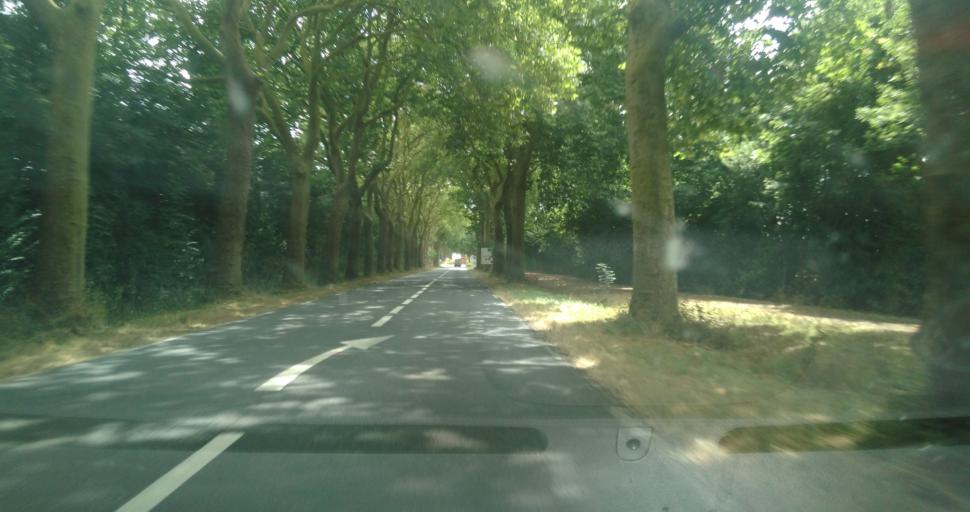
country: FR
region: Pays de la Loire
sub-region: Departement de la Vendee
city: Sainte-Hermine
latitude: 46.5608
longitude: -1.0715
